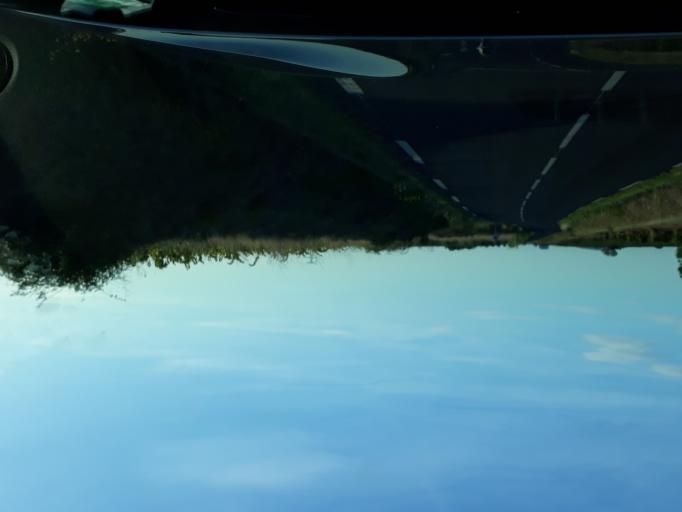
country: FR
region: Languedoc-Roussillon
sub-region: Departement de l'Herault
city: Pinet
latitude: 43.4129
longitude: 3.4888
